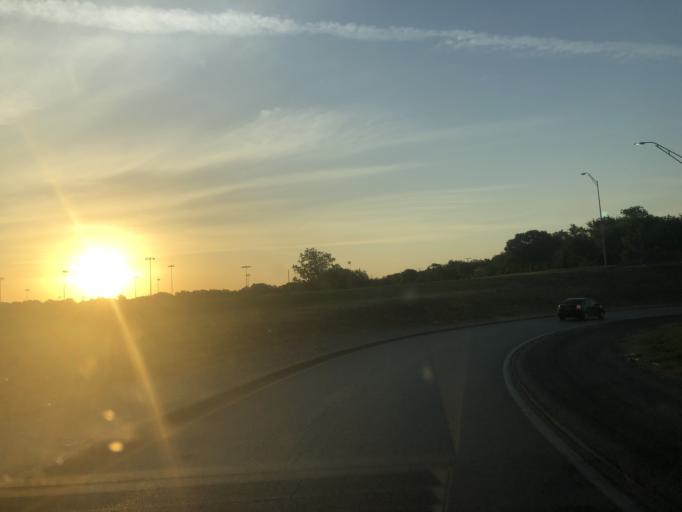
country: US
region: Texas
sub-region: Tarrant County
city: Sansom Park
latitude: 32.8096
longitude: -97.4170
